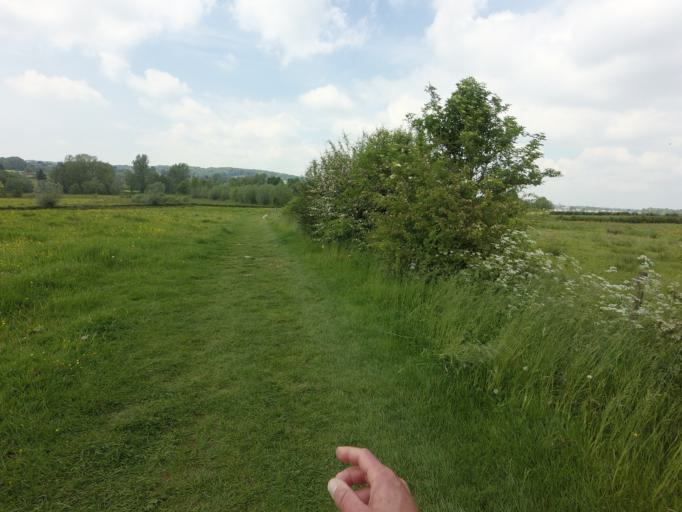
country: BE
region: Wallonia
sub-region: Province de Liege
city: Plombieres
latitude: 50.7833
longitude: 5.9226
